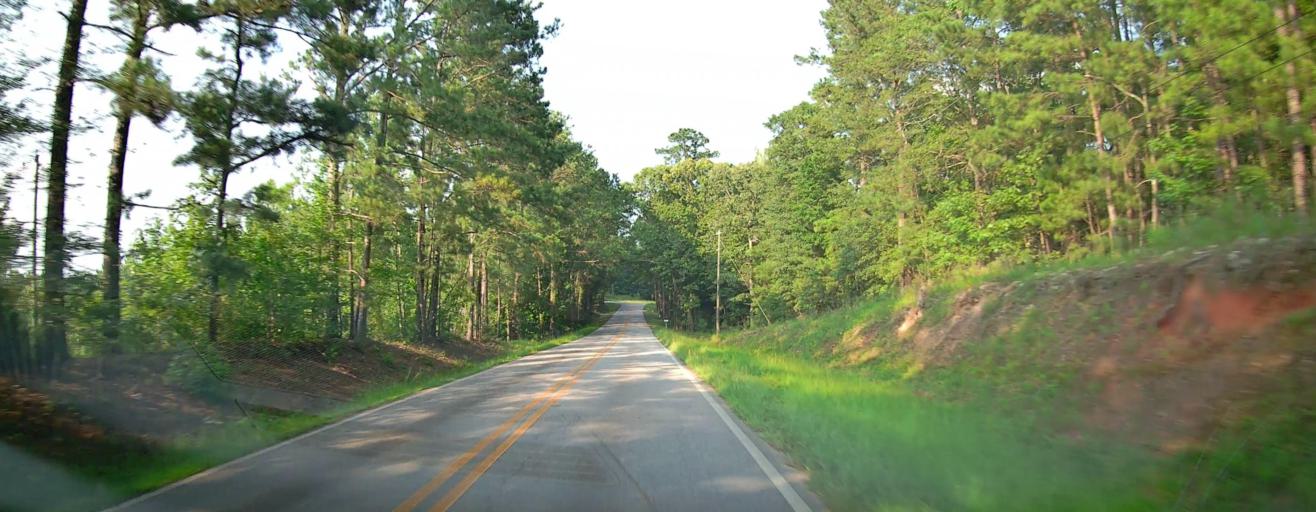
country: US
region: Georgia
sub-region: Monroe County
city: Forsyth
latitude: 32.9891
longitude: -83.7765
